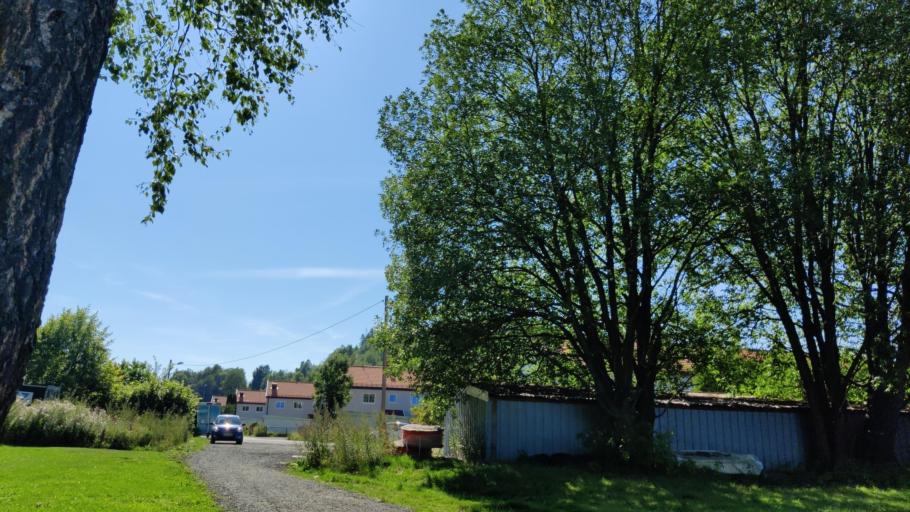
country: NO
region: Akershus
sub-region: Baerum
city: Lysaker
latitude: 59.9366
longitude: 10.6124
